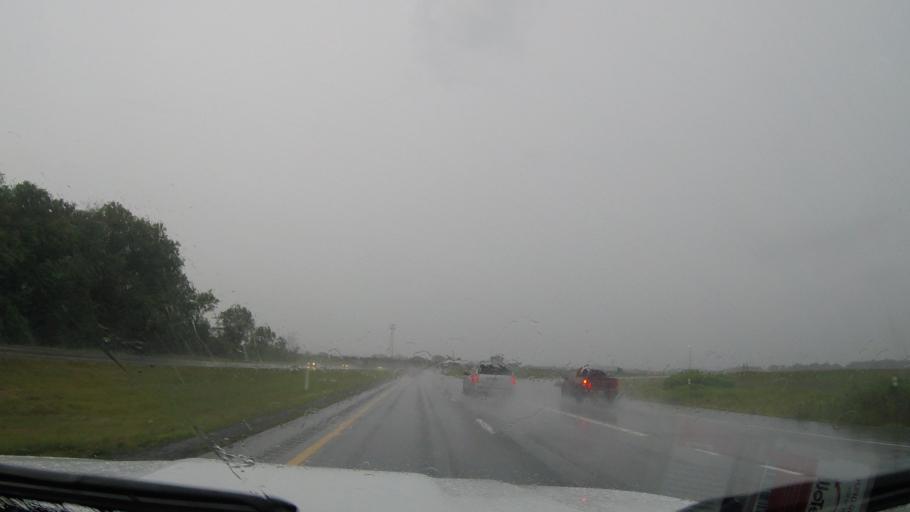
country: US
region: New York
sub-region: Seneca County
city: Waterloo
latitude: 42.9668
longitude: -76.8563
